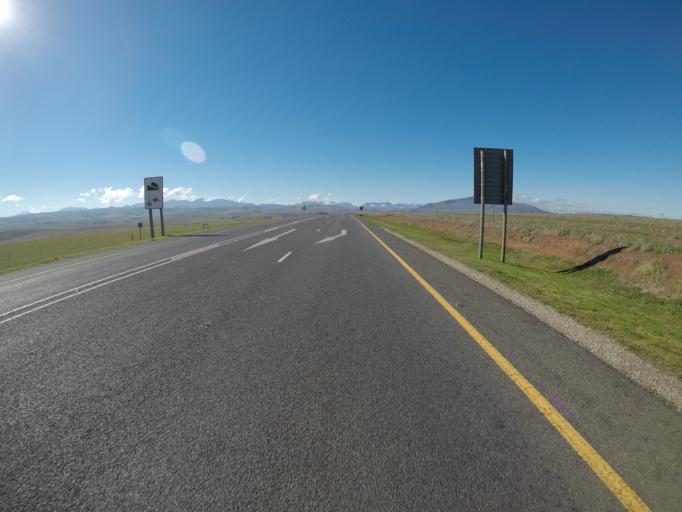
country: ZA
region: Western Cape
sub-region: Overberg District Municipality
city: Caledon
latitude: -34.2188
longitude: 19.3144
